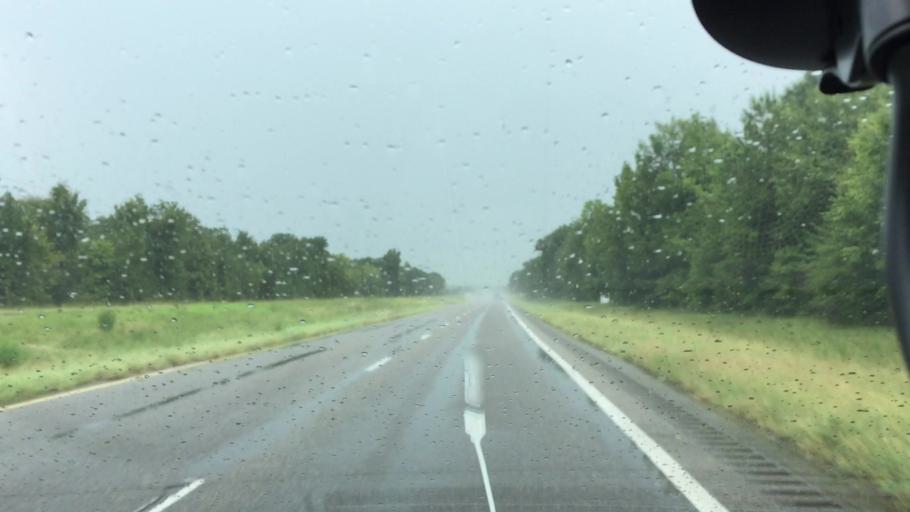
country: US
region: Alabama
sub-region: Montgomery County
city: Pike Road
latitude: 32.2416
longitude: -86.1327
